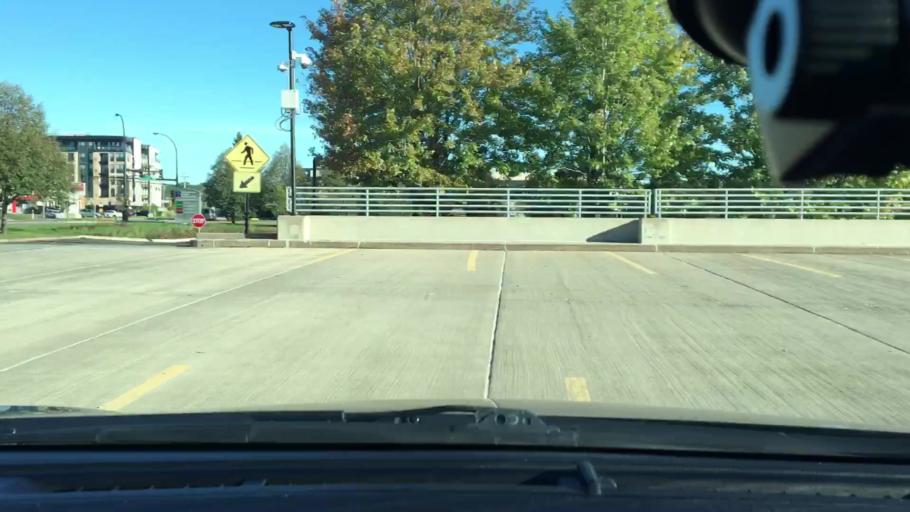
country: US
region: Minnesota
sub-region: Hennepin County
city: Minnetonka Mills
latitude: 44.9647
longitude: -93.4417
